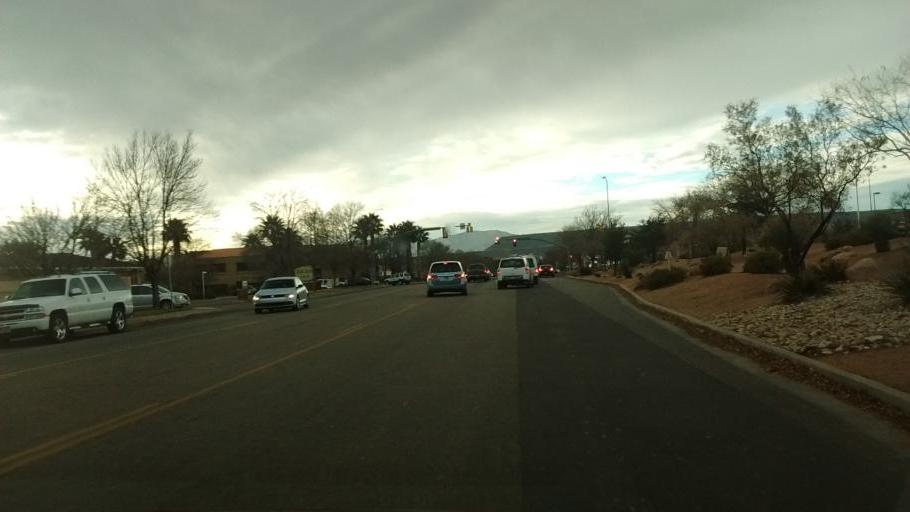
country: US
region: Utah
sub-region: Washington County
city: Saint George
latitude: 37.0963
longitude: -113.5558
